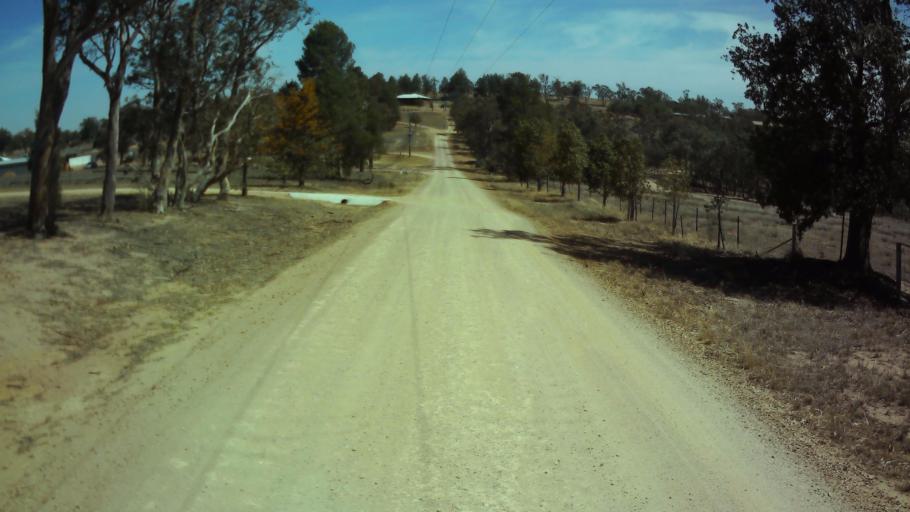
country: AU
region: New South Wales
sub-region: Weddin
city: Grenfell
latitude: -33.9127
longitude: 148.1560
